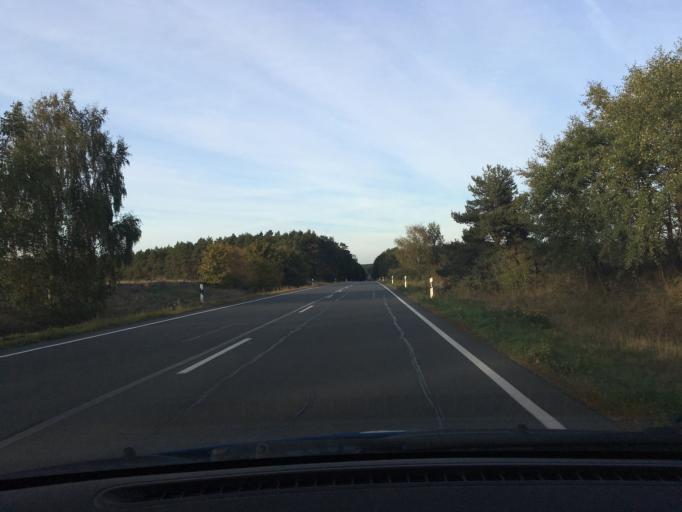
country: DE
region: Lower Saxony
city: Betzendorf
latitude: 53.1540
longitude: 10.2980
